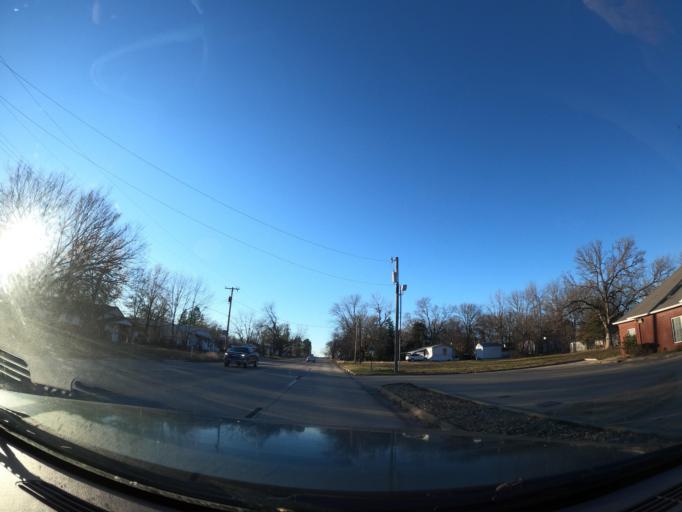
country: US
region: Oklahoma
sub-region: Pittsburg County
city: Hartshorne
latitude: 34.8425
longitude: -95.5478
